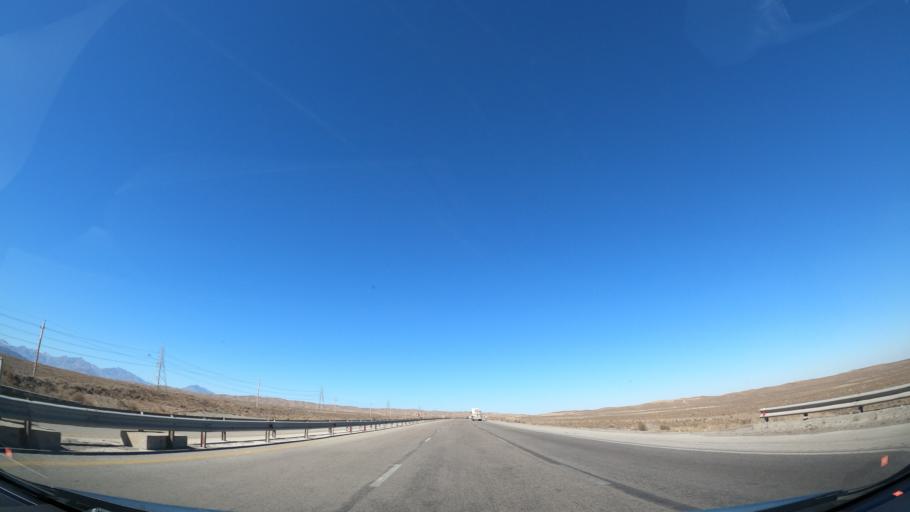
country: IR
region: Isfahan
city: Kashan
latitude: 33.7654
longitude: 51.6663
